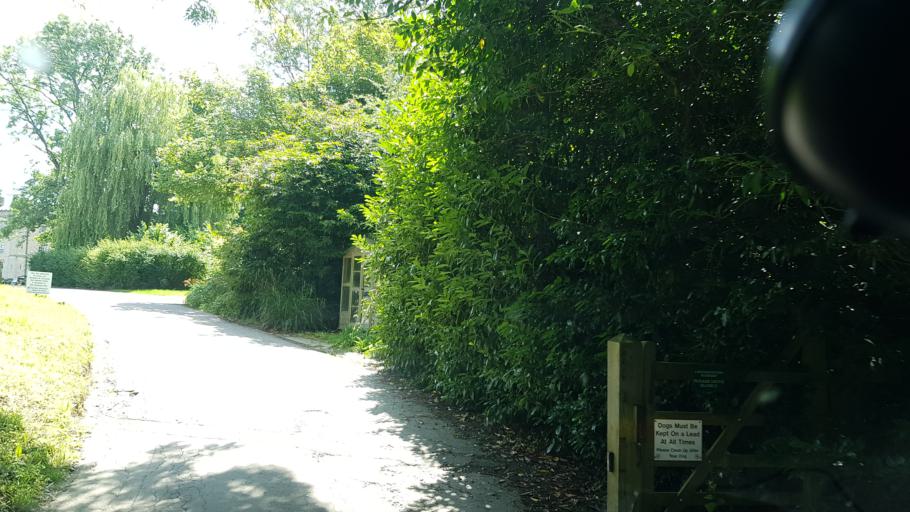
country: GB
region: England
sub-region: Kent
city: Edenbridge
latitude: 51.1870
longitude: 0.1410
